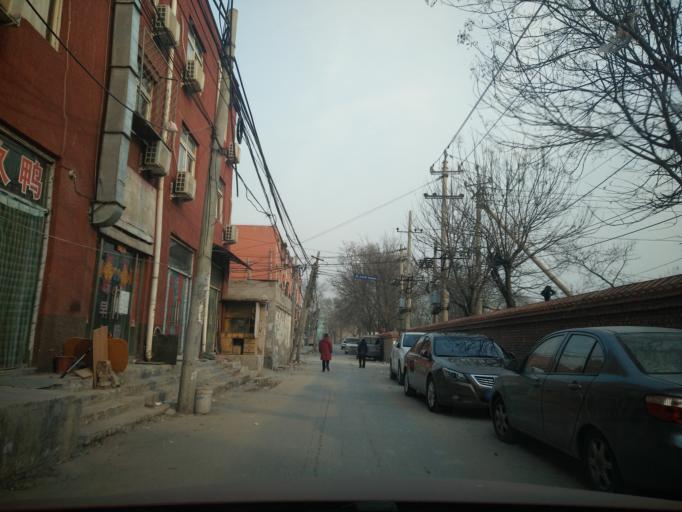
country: CN
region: Beijing
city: Jiugong
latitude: 39.8011
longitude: 116.4320
